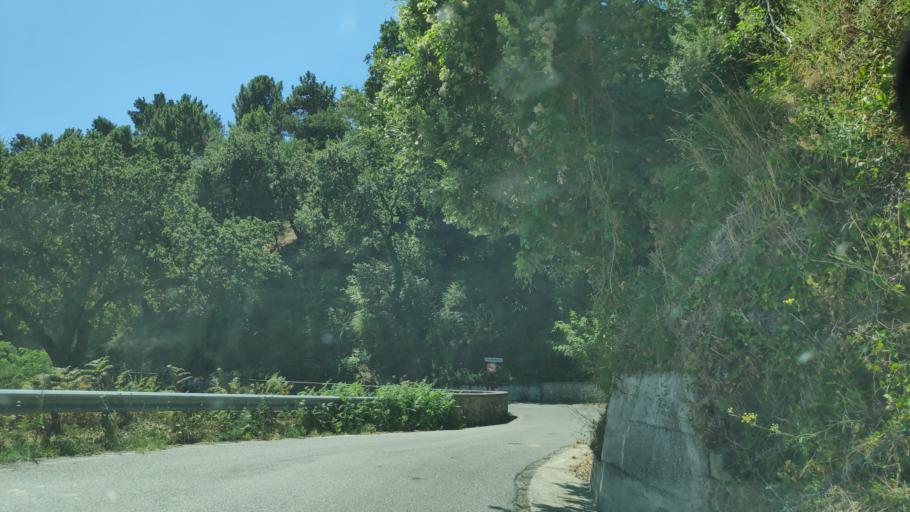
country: IT
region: Calabria
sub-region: Provincia di Catanzaro
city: Gasperina
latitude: 38.7422
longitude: 16.5074
